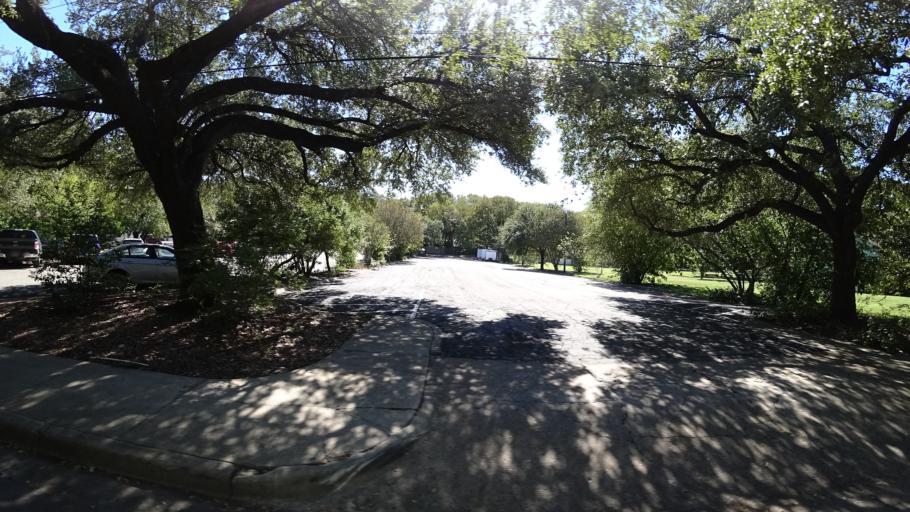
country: US
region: Texas
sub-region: Travis County
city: West Lake Hills
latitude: 30.3093
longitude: -97.7645
